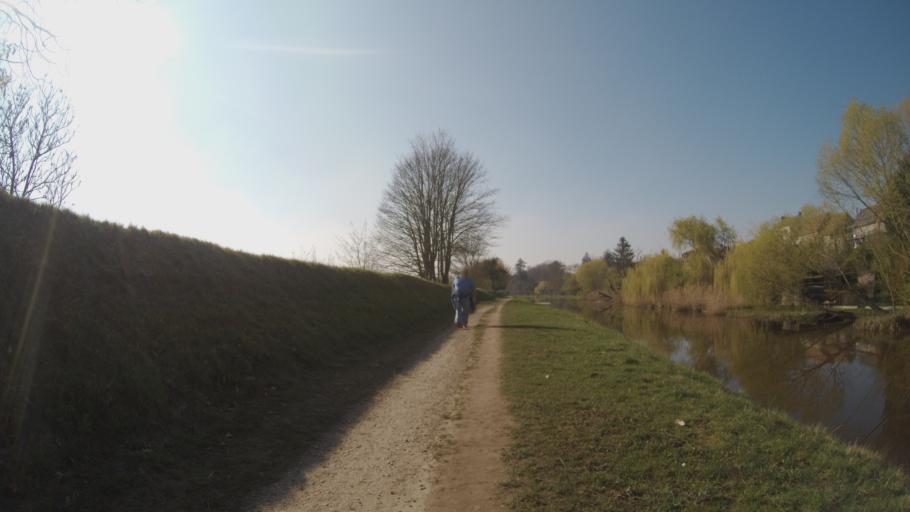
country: FR
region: Centre
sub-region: Departement du Loiret
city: Checy
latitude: 47.8904
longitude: 2.0239
